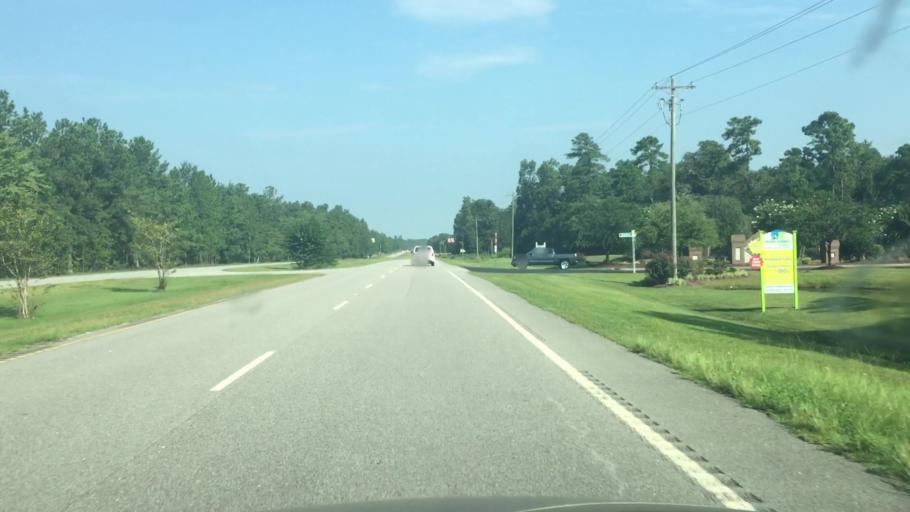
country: US
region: South Carolina
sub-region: Horry County
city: Loris
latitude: 34.0543
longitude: -78.8411
